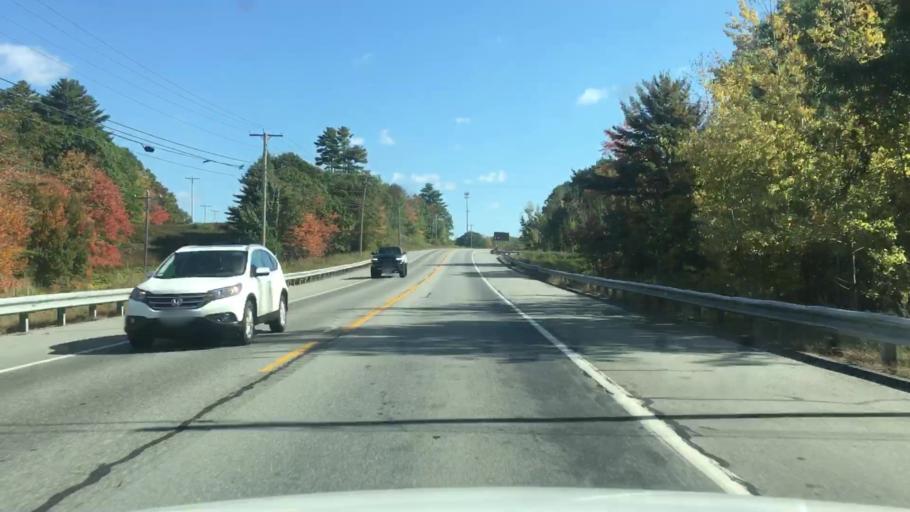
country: US
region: Maine
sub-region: Knox County
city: Warren
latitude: 44.1206
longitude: -69.2807
